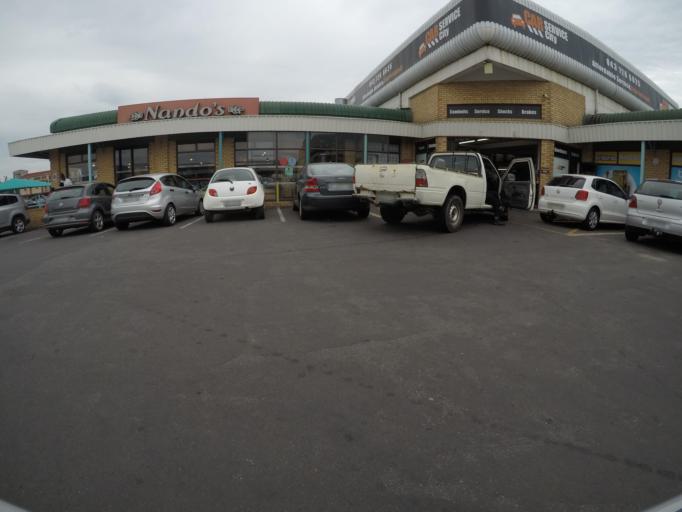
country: ZA
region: Eastern Cape
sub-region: Buffalo City Metropolitan Municipality
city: East London
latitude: -32.9835
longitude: 27.8996
